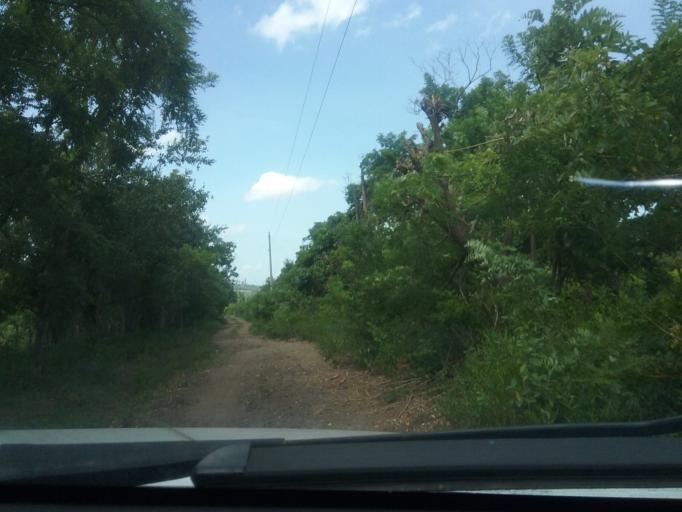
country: NI
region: Matagalpa
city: Terrabona
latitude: 12.6674
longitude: -85.9840
